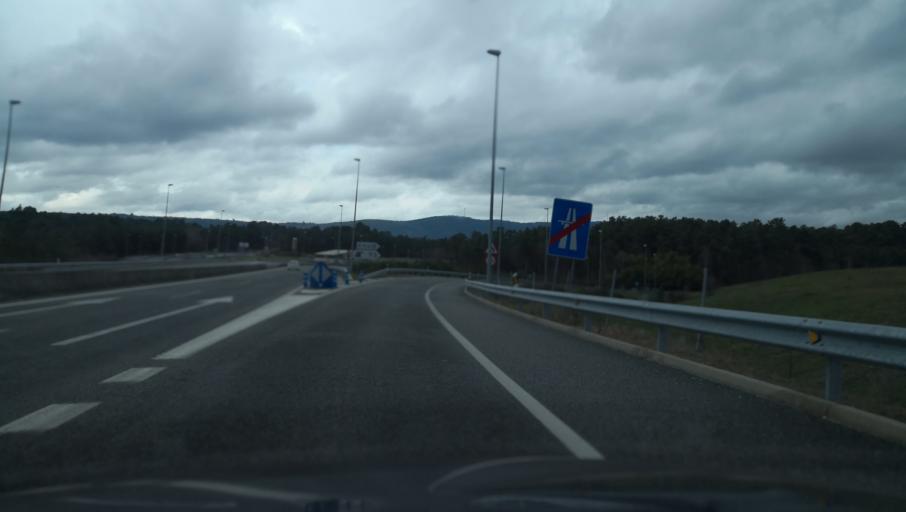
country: ES
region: Galicia
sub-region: Provincia de Ourense
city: Maside
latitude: 42.4471
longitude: -8.0207
